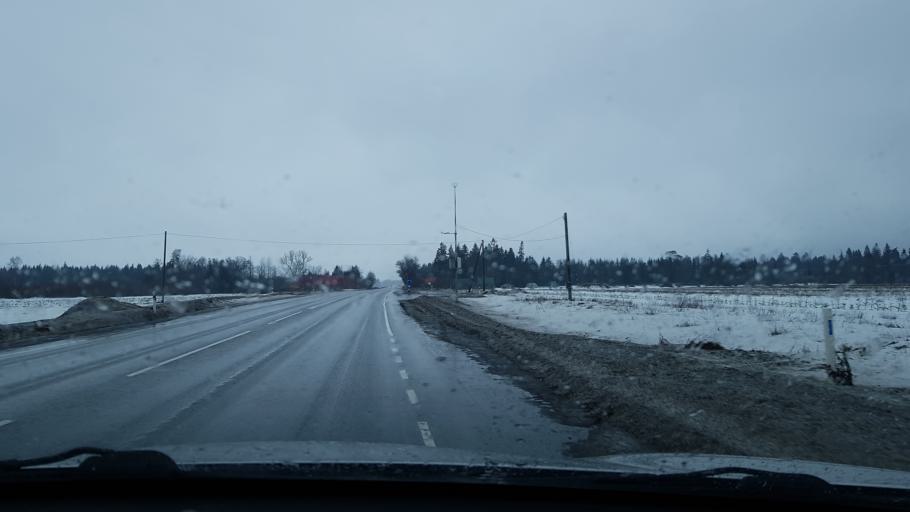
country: EE
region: Raplamaa
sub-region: Kohila vald
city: Kohila
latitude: 59.1993
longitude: 24.7840
